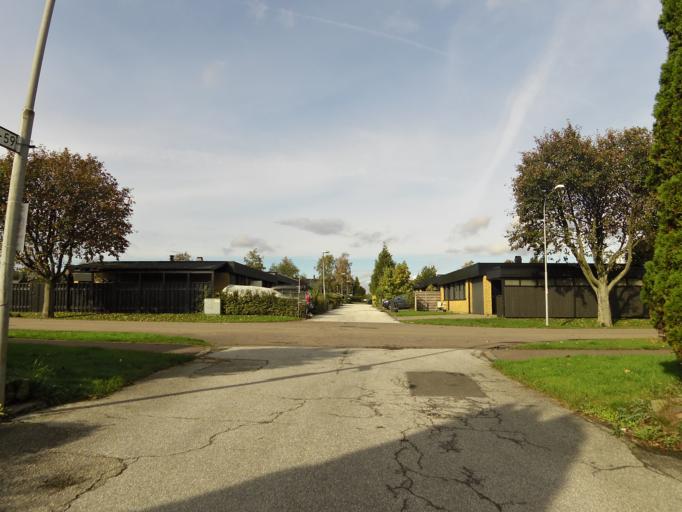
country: SE
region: Skane
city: Bjarred
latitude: 55.7162
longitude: 13.0369
